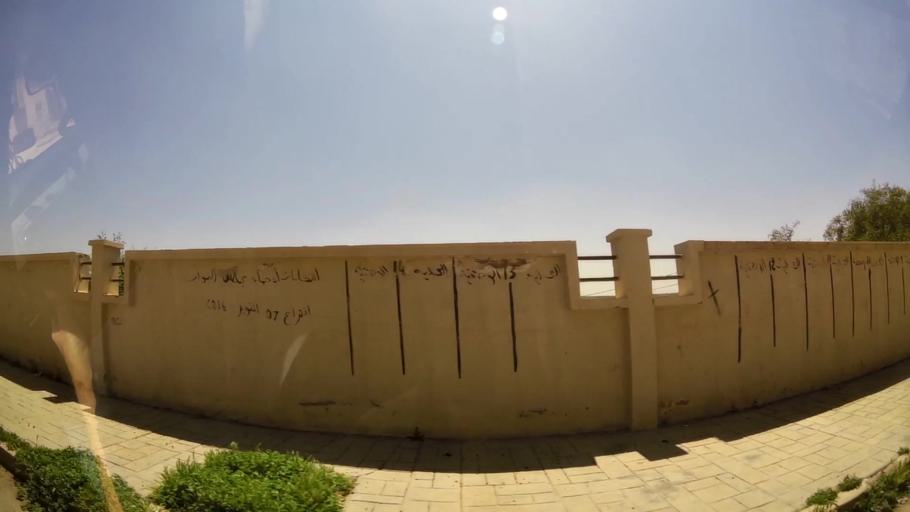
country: MA
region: Oriental
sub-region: Oujda-Angad
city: Oujda
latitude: 34.6787
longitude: -1.9605
